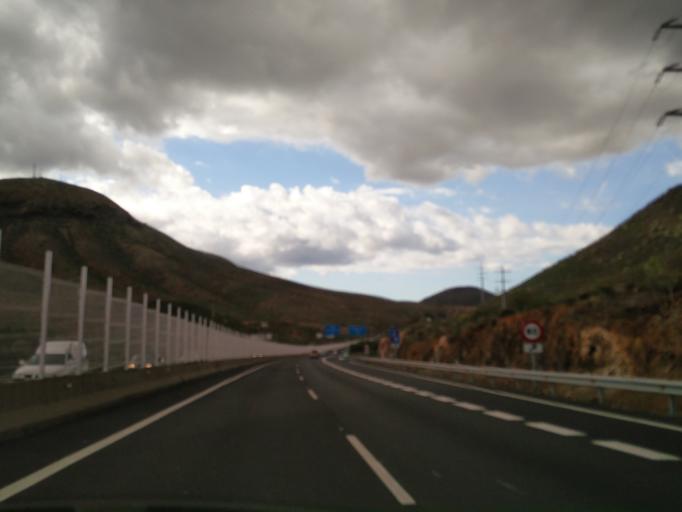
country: ES
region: Canary Islands
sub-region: Provincia de Santa Cruz de Tenerife
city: Las Rosas
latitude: 28.0523
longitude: -16.6750
